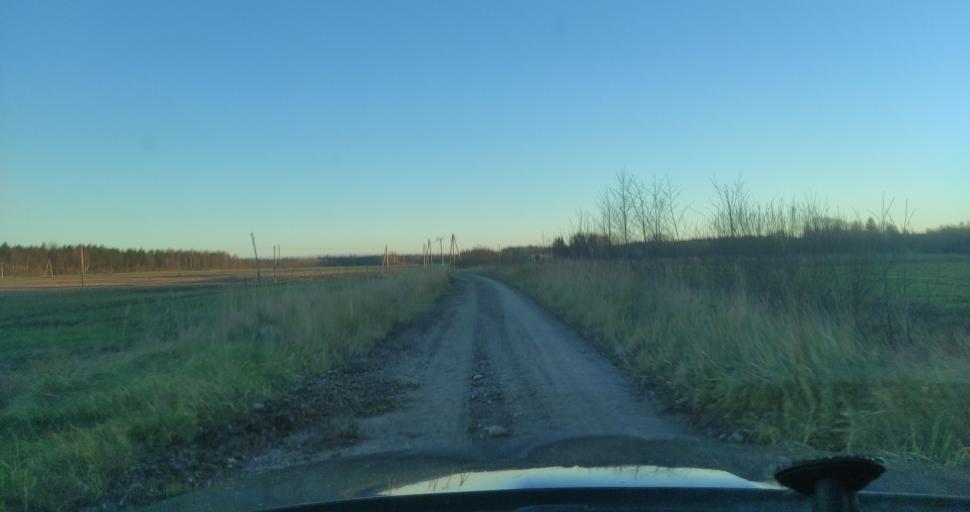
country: LV
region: Dundaga
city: Dundaga
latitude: 57.3881
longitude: 22.0872
